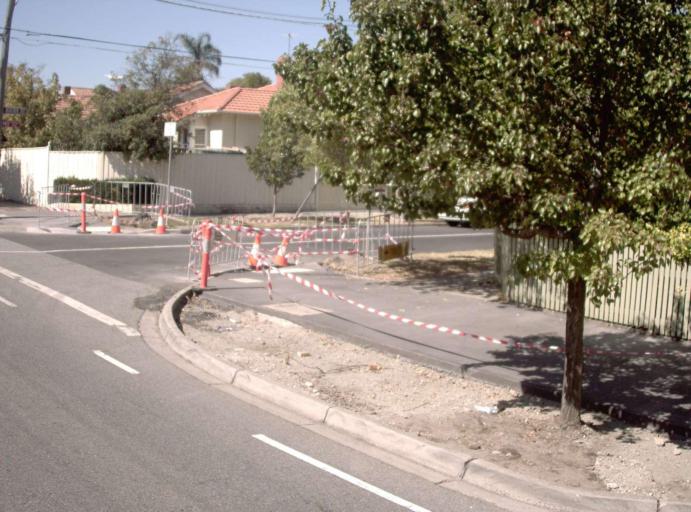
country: AU
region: Victoria
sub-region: Bayside
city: Hampton
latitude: -37.9305
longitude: 145.0038
